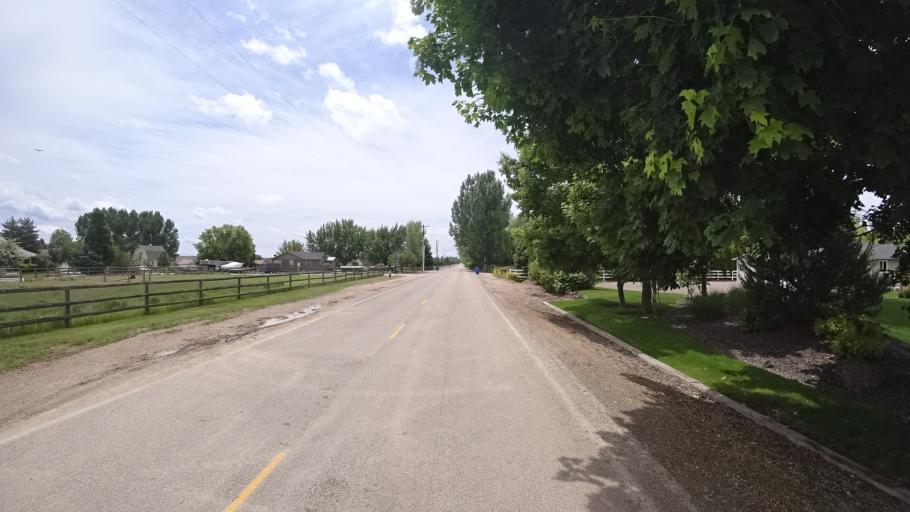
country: US
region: Idaho
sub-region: Ada County
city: Eagle
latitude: 43.7170
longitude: -116.4035
